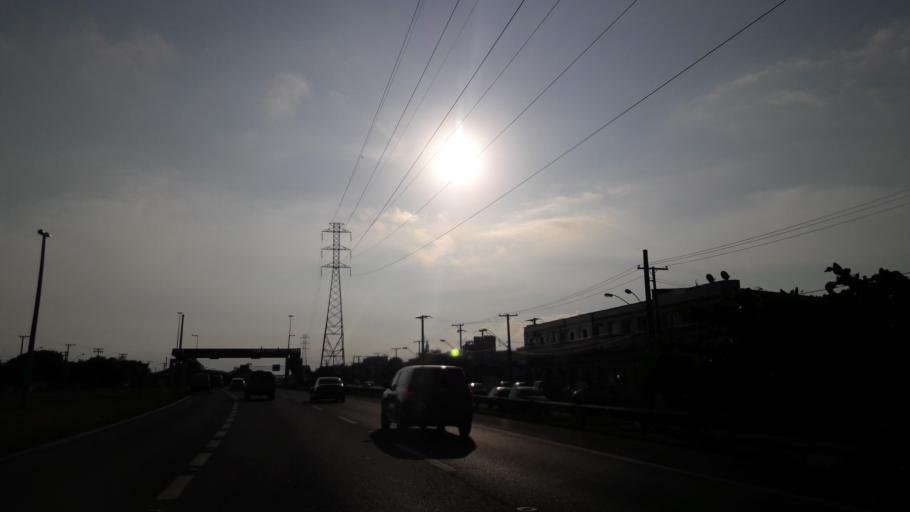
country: BR
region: Sao Paulo
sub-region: Mongagua
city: Mongagua
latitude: -24.1252
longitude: -46.6839
